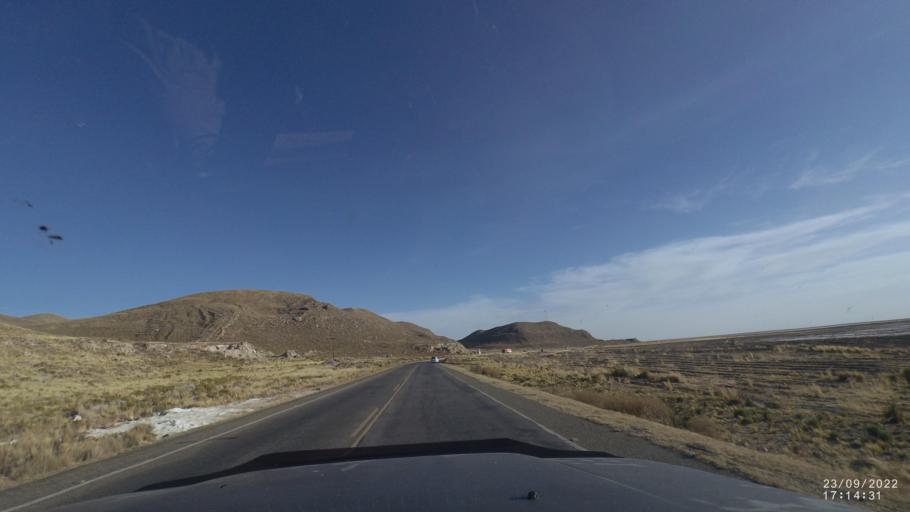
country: BO
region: Oruro
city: Challapata
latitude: -18.7229
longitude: -66.8667
